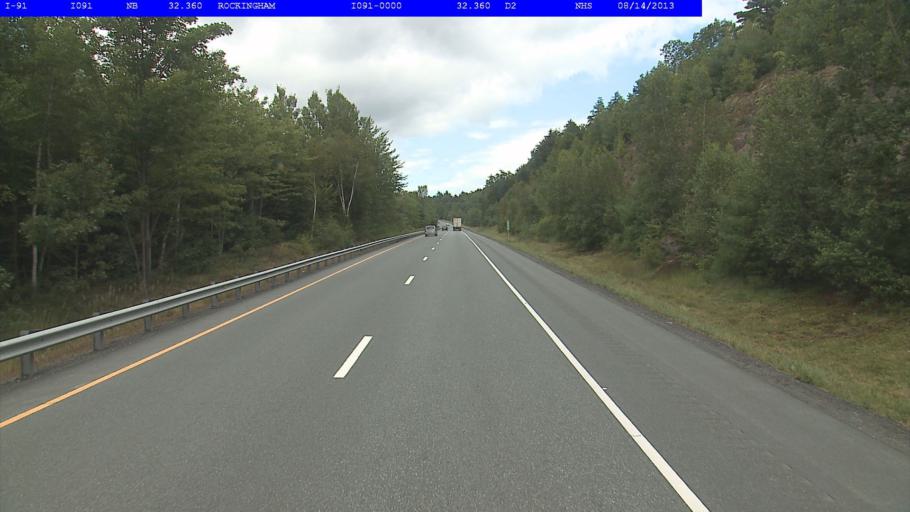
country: US
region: Vermont
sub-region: Windham County
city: Bellows Falls
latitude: 43.1406
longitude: -72.4753
